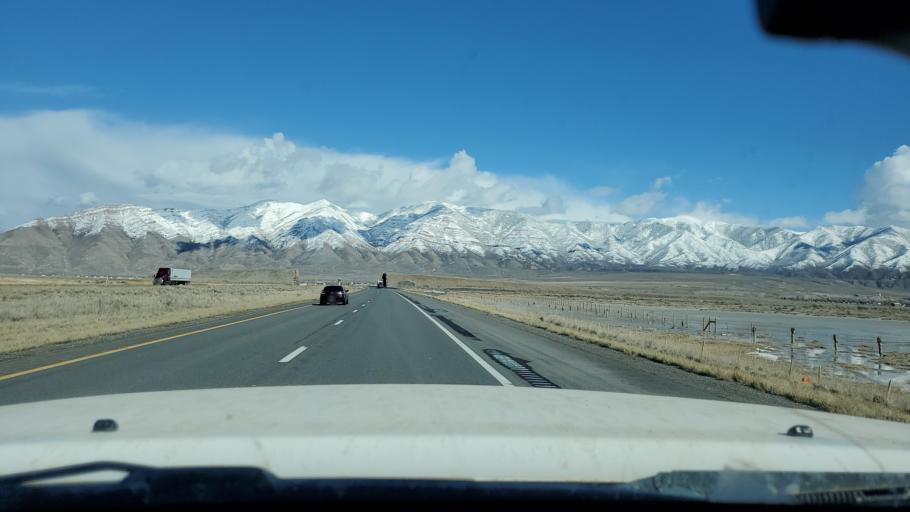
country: US
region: Utah
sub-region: Tooele County
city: Stansbury park
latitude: 40.6615
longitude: -112.3384
